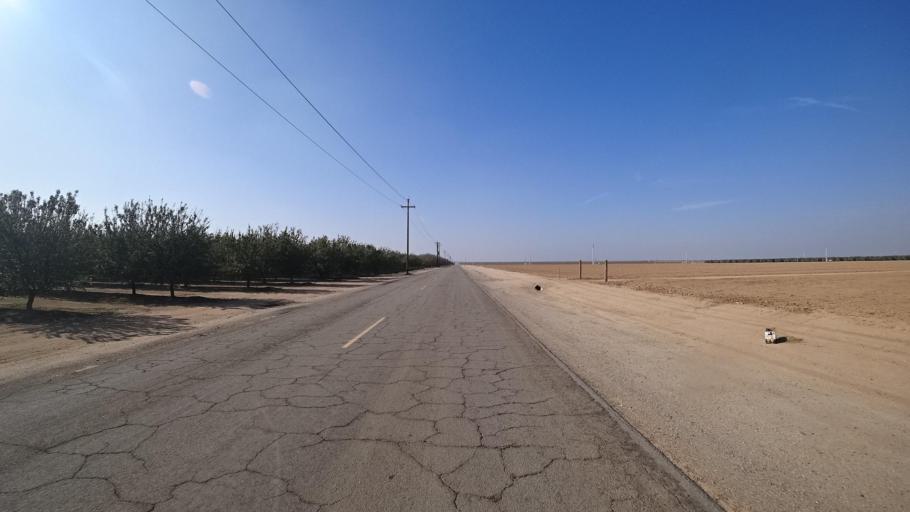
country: US
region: California
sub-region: Kern County
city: Shafter
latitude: 35.5304
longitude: -119.1367
